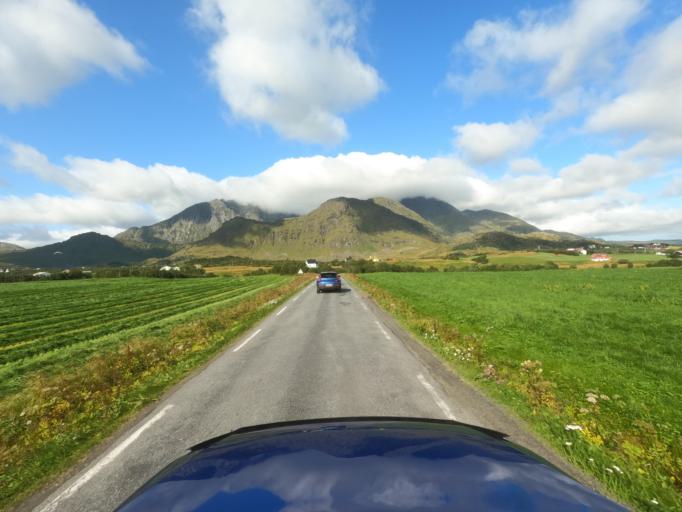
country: NO
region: Nordland
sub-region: Vestvagoy
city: Leknes
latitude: 68.1822
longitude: 13.6183
